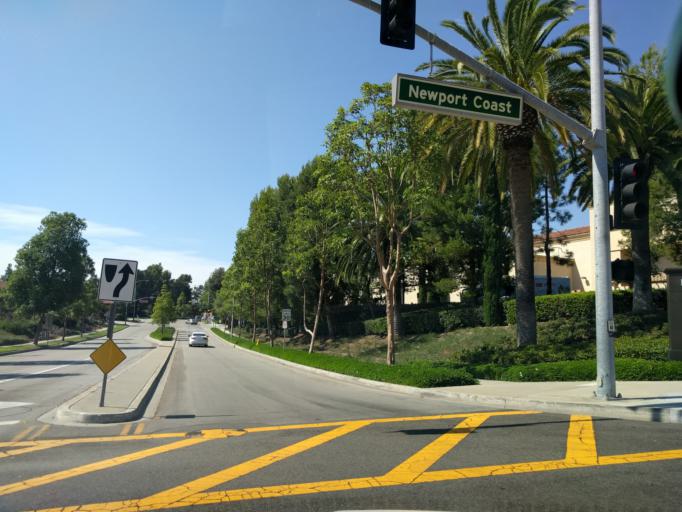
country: US
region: California
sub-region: Orange County
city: San Joaquin Hills
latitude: 33.6058
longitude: -117.8274
